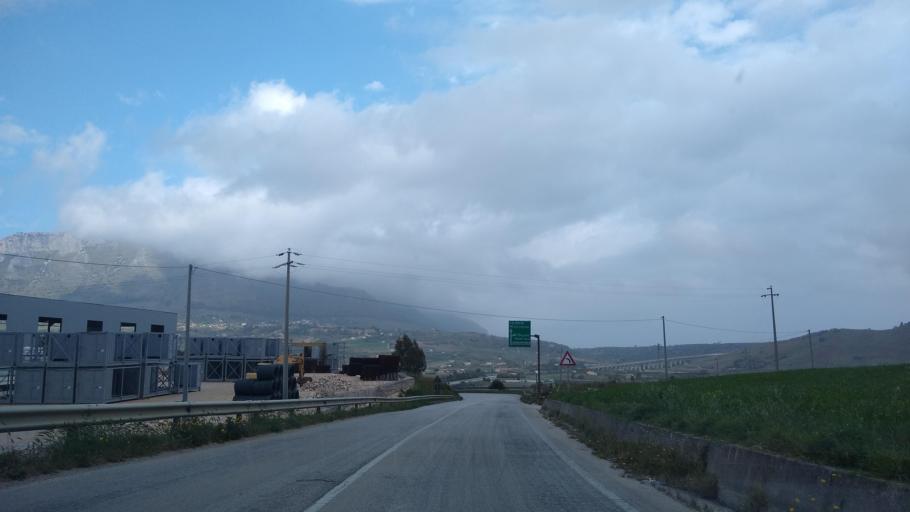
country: IT
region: Sicily
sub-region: Trapani
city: Alcamo
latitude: 37.9711
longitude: 12.9287
